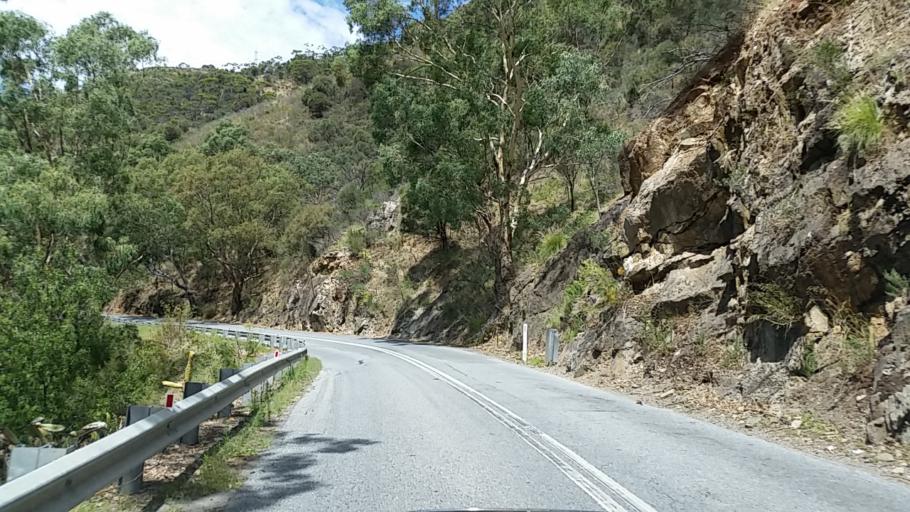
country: AU
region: South Australia
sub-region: Campbelltown
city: Athelstone
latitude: -34.8588
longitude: 138.7322
